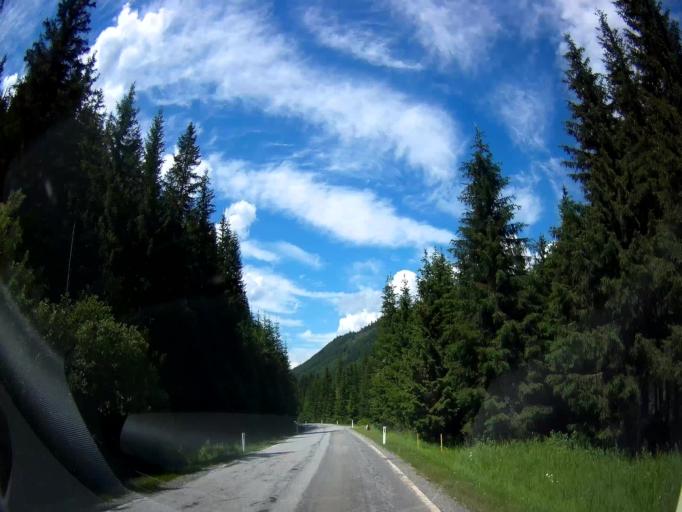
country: AT
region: Styria
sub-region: Politischer Bezirk Murau
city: Stadl an der Mur
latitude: 46.9960
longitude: 14.0151
